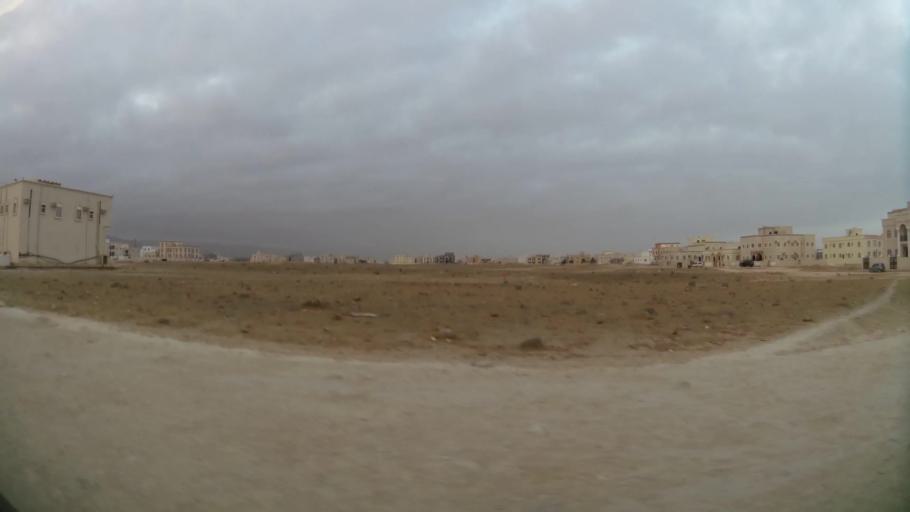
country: OM
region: Zufar
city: Salalah
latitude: 17.0391
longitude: 54.0338
